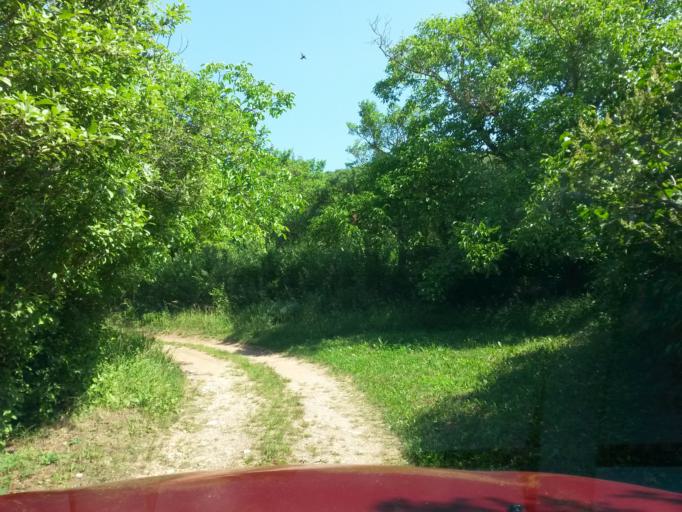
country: SK
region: Kosicky
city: Medzev
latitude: 48.6093
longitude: 20.8691
